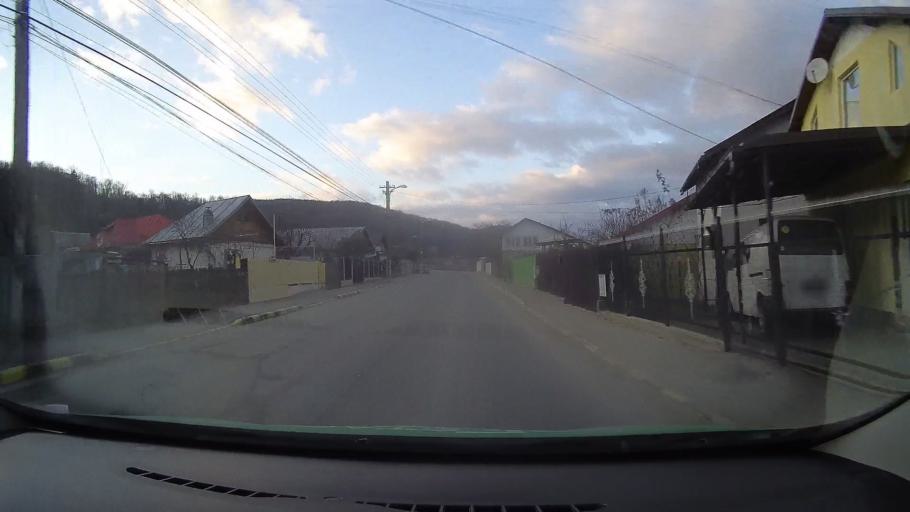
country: RO
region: Dambovita
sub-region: Municipiul Moreni
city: Moreni
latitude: 44.9899
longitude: 25.6375
